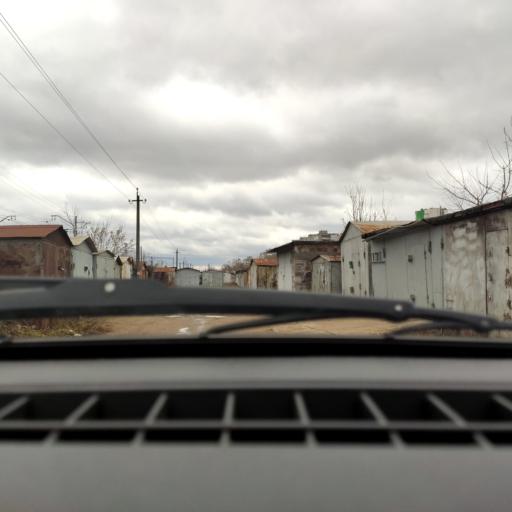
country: RU
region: Bashkortostan
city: Ufa
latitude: 54.8190
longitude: 56.1320
